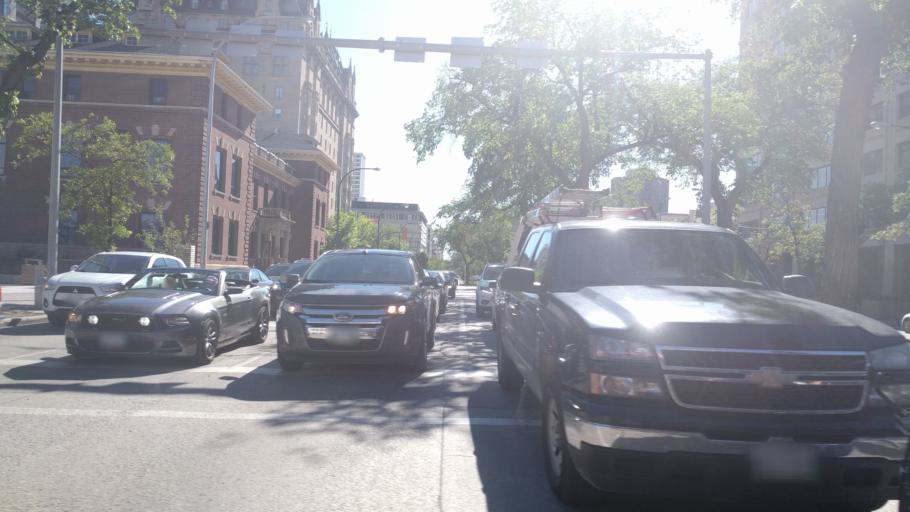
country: CA
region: Manitoba
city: Winnipeg
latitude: 49.8891
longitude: -97.1354
